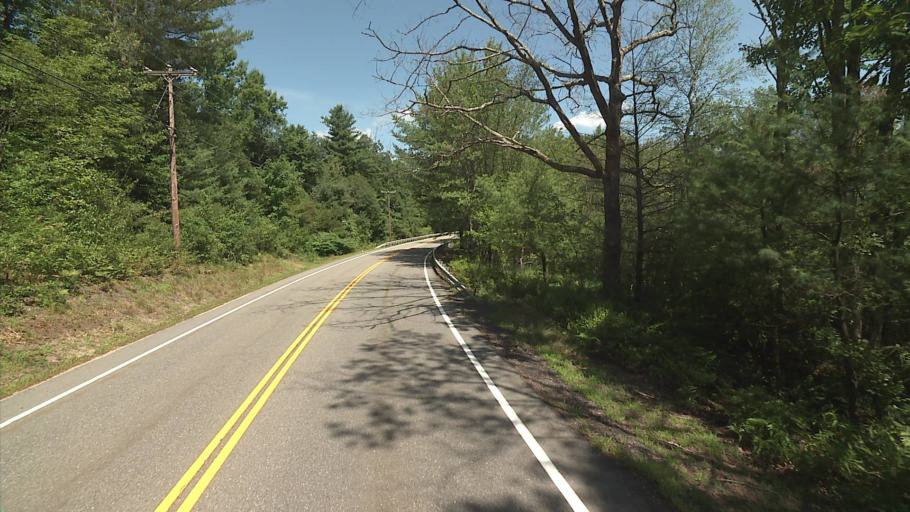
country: US
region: Massachusetts
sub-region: Worcester County
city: Southbridge
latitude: 41.9769
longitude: -72.0855
